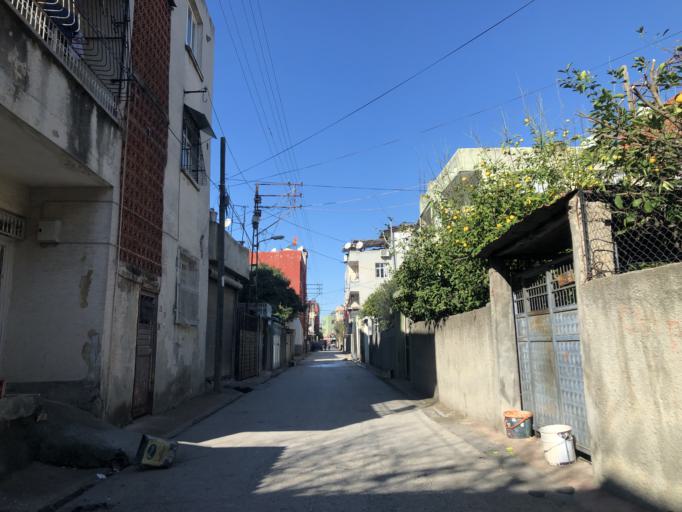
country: TR
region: Adana
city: Yuregir
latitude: 37.0072
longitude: 35.3664
